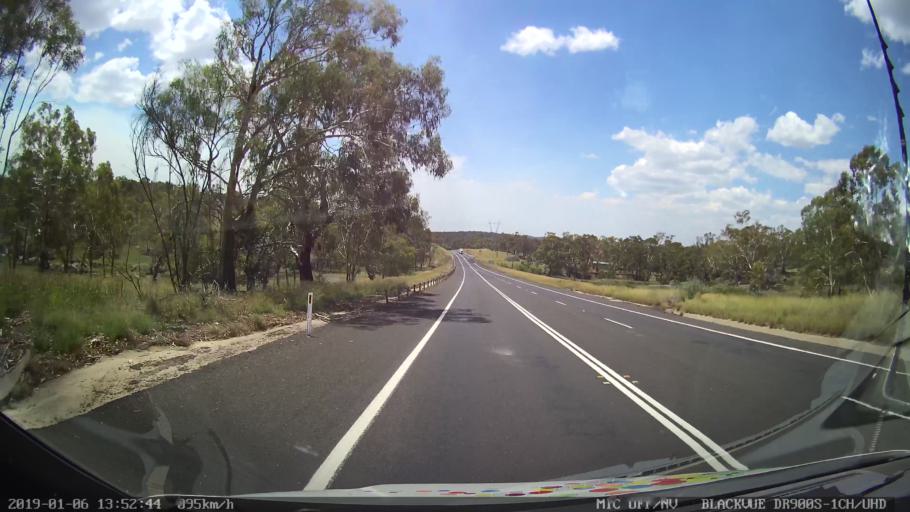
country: AU
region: New South Wales
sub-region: Tamworth Municipality
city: Kootingal
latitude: -30.9168
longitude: 151.1340
